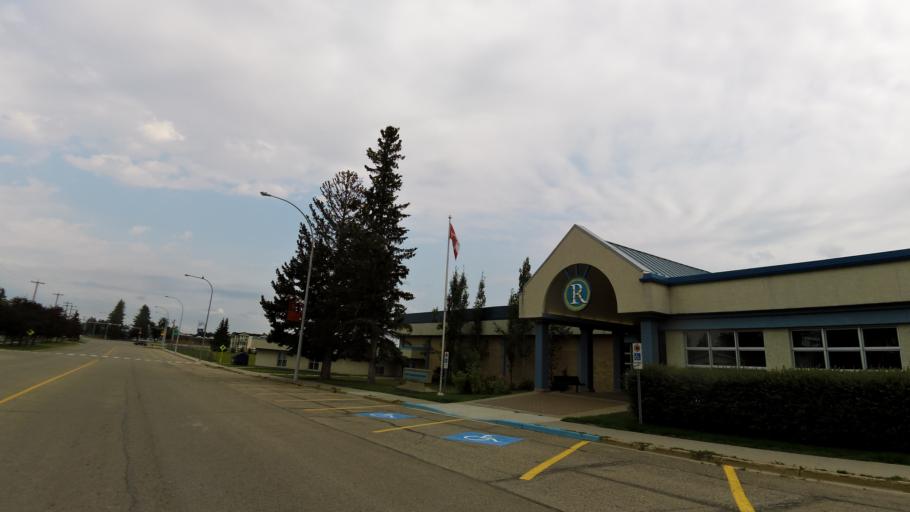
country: CA
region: Alberta
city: Rocky Mountain House
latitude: 52.3744
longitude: -114.9160
